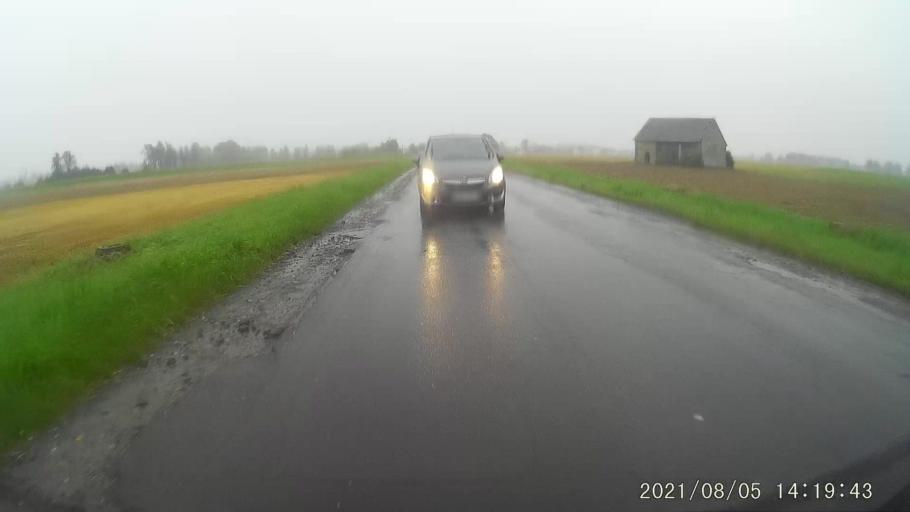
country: PL
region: Opole Voivodeship
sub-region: Powiat prudnicki
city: Biala
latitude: 50.4675
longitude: 17.6850
